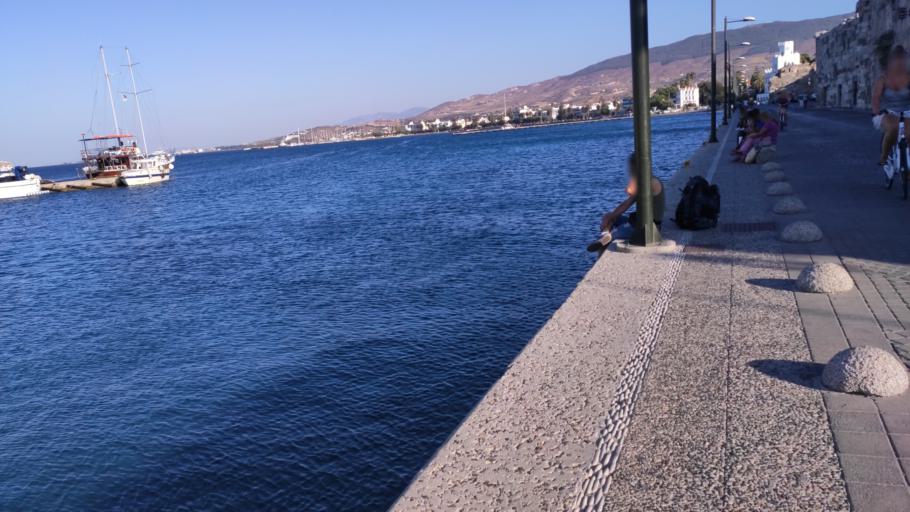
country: GR
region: South Aegean
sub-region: Nomos Dodekanisou
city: Kos
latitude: 36.8976
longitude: 27.2902
